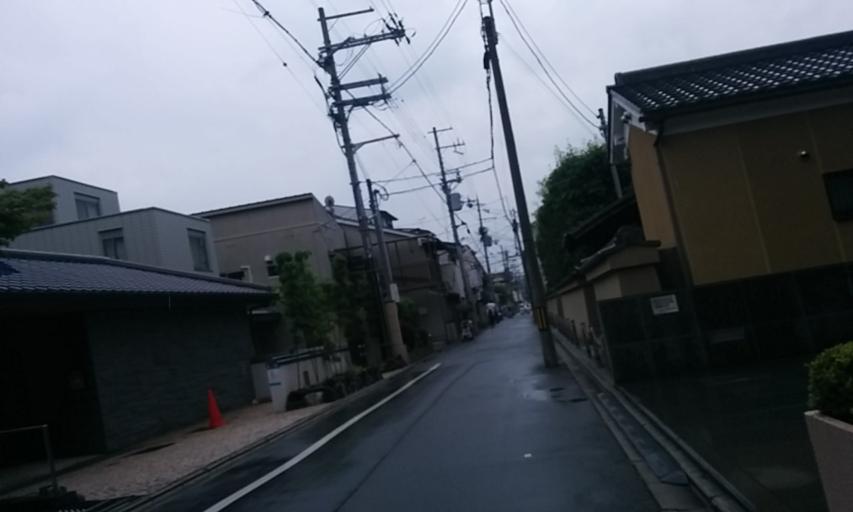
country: JP
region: Kyoto
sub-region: Kyoto-shi
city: Kamigyo-ku
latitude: 35.0379
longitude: 135.7607
